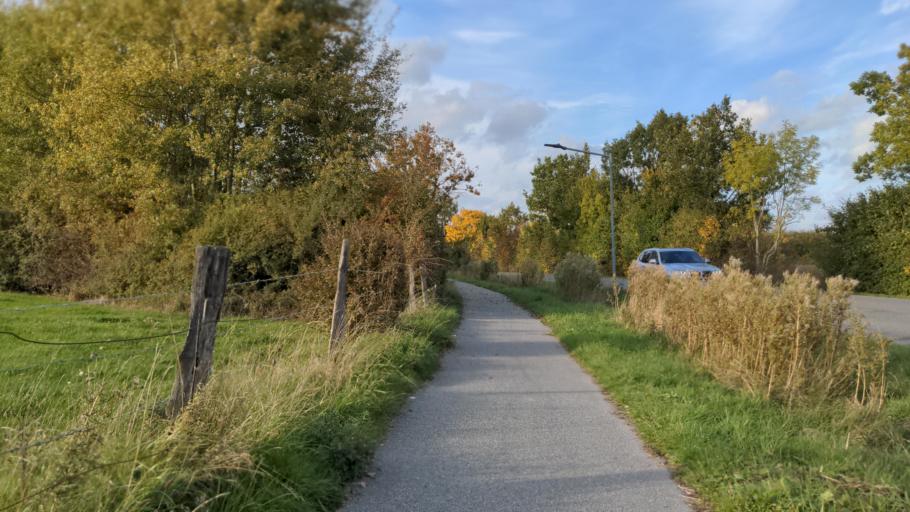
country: DE
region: Schleswig-Holstein
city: Ahrensbok
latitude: 54.0054
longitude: 10.5832
